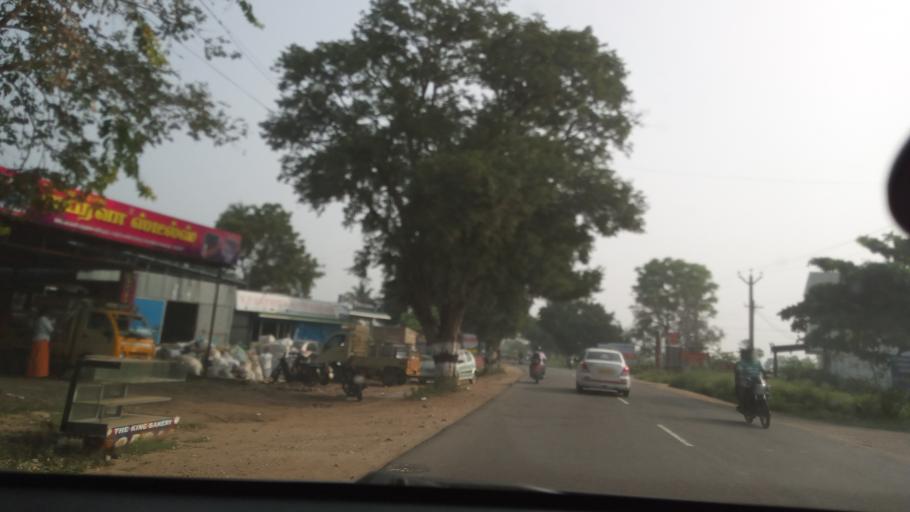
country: IN
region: Tamil Nadu
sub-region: Coimbatore
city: Periyanayakkanpalaiyam
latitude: 11.1459
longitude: 77.0426
